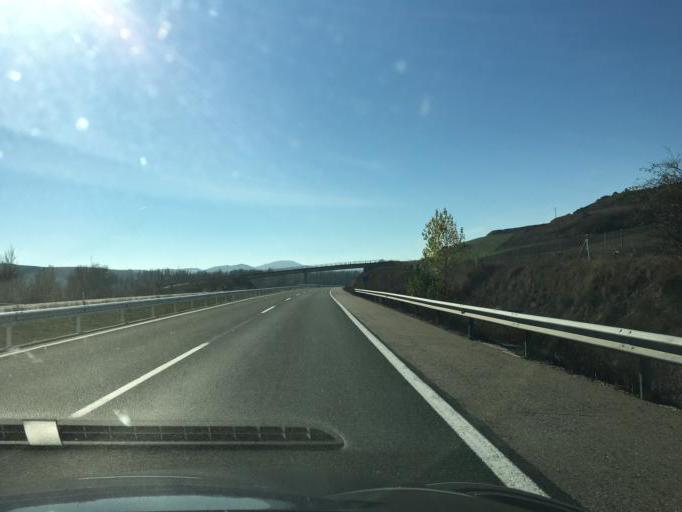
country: ES
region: Castille and Leon
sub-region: Provincia de Burgos
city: Pradanos de Bureba
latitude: 42.5049
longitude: -3.3505
